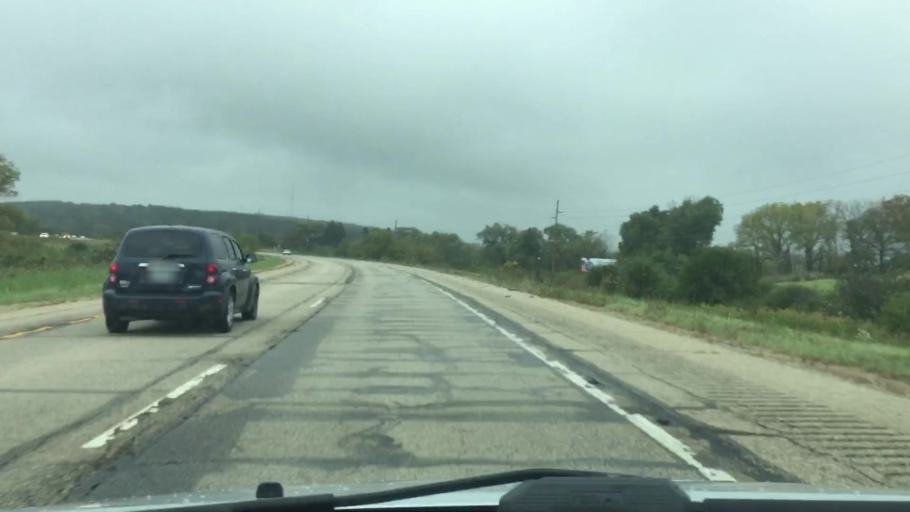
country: US
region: Wisconsin
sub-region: Walworth County
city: Como
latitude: 42.6180
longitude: -88.4591
